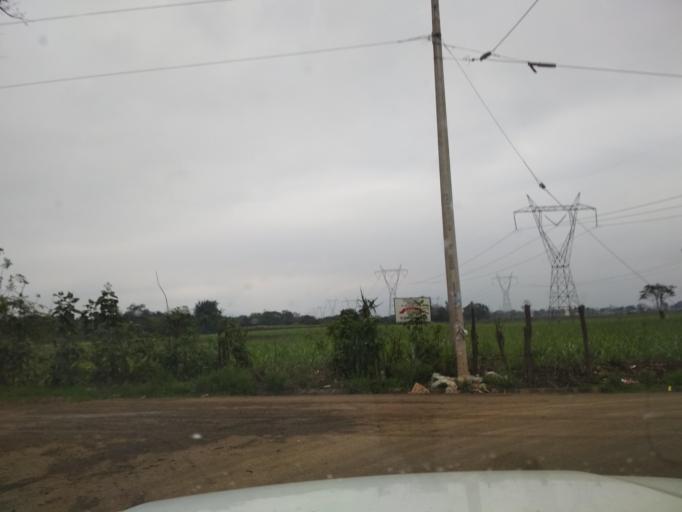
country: MX
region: Veracruz
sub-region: Cordoba
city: Veinte de Noviembre
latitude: 18.8657
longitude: -96.9607
